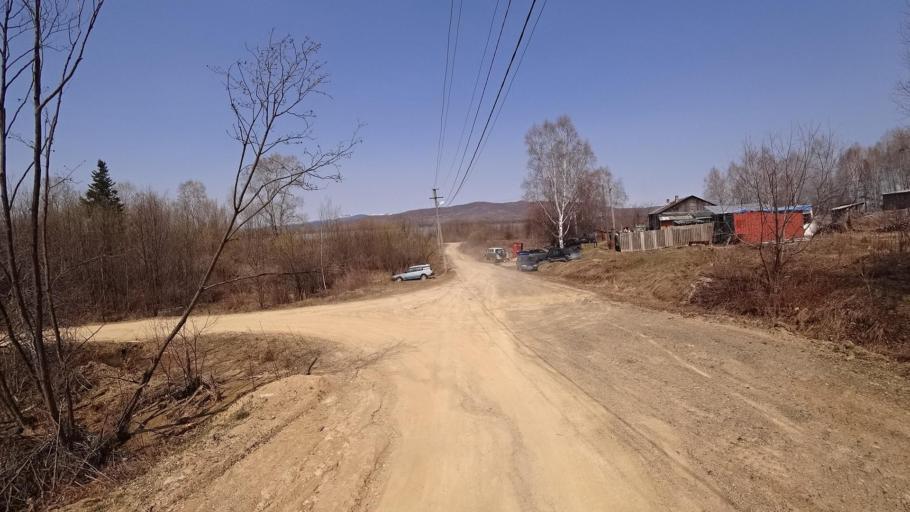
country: RU
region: Khabarovsk Krai
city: Selikhino
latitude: 50.6662
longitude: 137.4045
